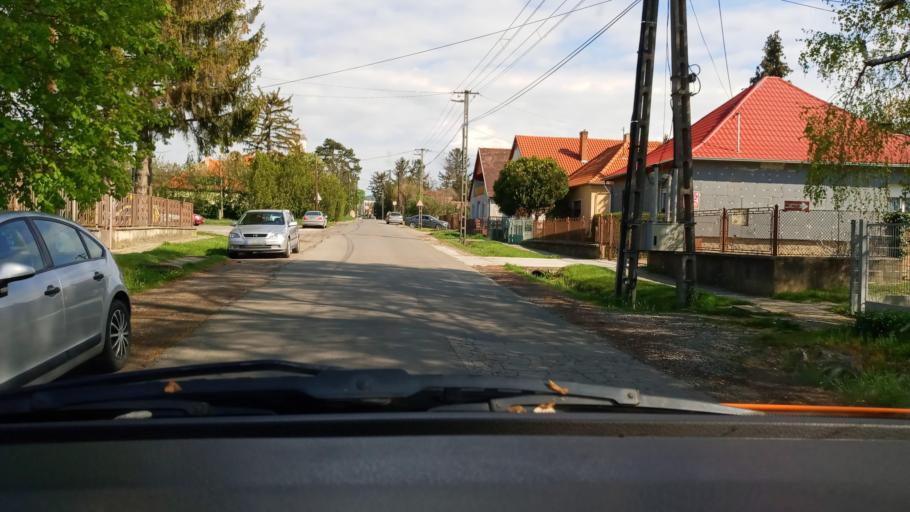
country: HU
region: Baranya
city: Hosszuheteny
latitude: 46.1168
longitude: 18.3408
